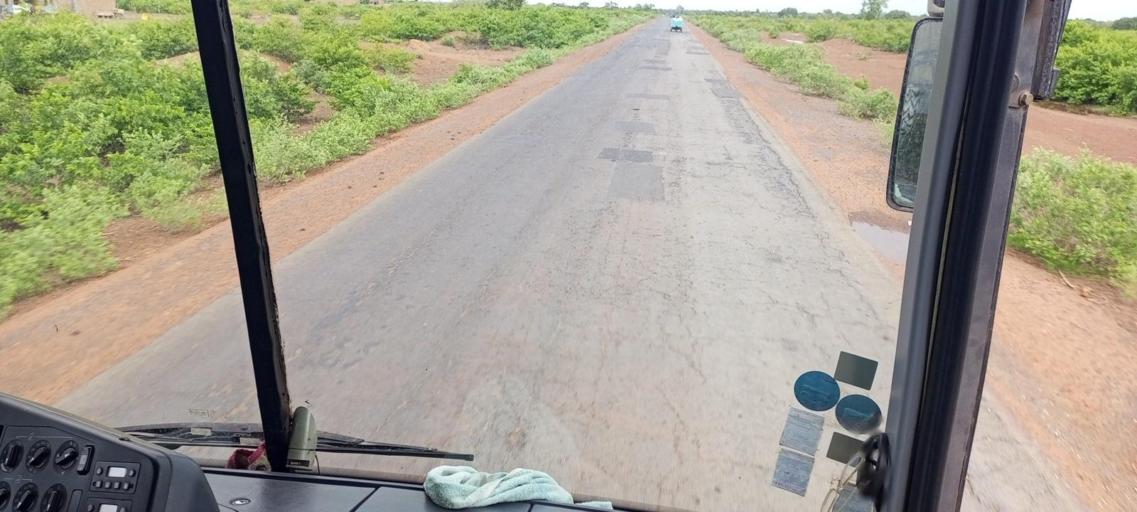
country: ML
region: Segou
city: Bla
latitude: 12.7563
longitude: -5.7360
